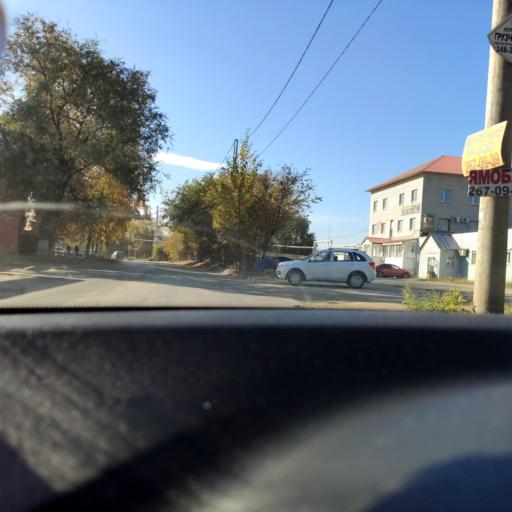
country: RU
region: Samara
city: Petra-Dubrava
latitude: 53.2441
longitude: 50.2993
